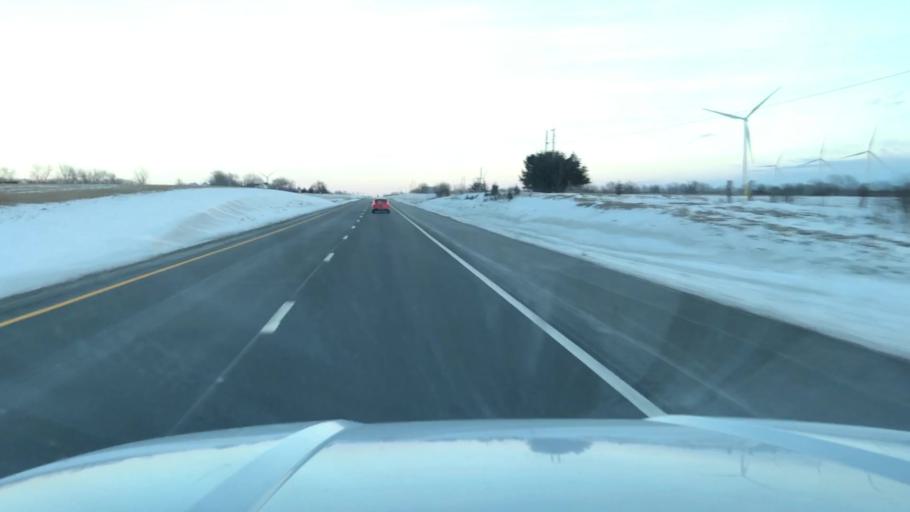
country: US
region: Missouri
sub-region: DeKalb County
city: Maysville
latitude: 39.7616
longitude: -94.4177
